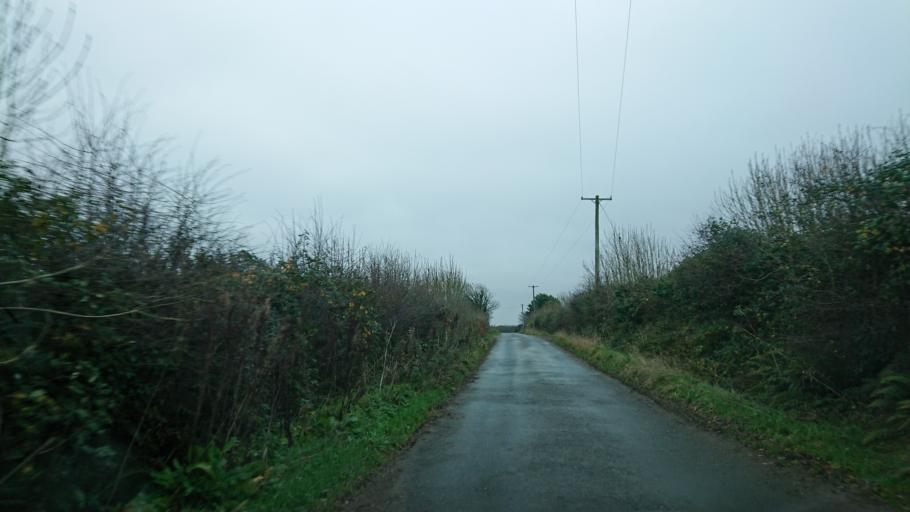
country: IE
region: Munster
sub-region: Waterford
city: Dunmore East
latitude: 52.1982
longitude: -7.0050
